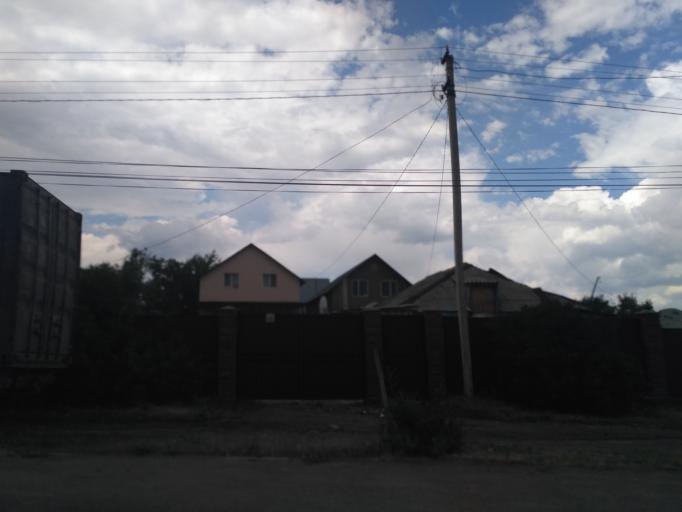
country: KZ
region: Almaty Oblysy
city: Burunday
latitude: 43.2066
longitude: 76.6373
